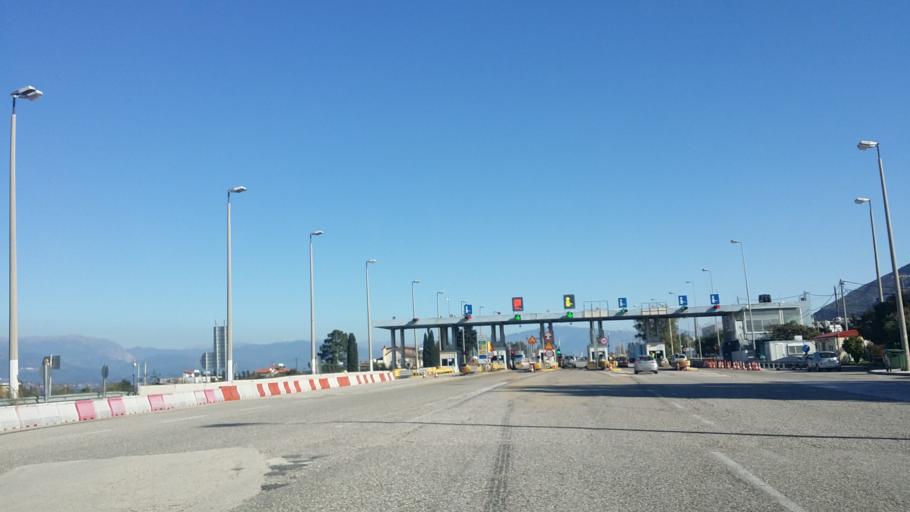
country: GR
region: West Greece
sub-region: Nomos Achaias
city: Rio
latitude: 38.3026
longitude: 21.8005
